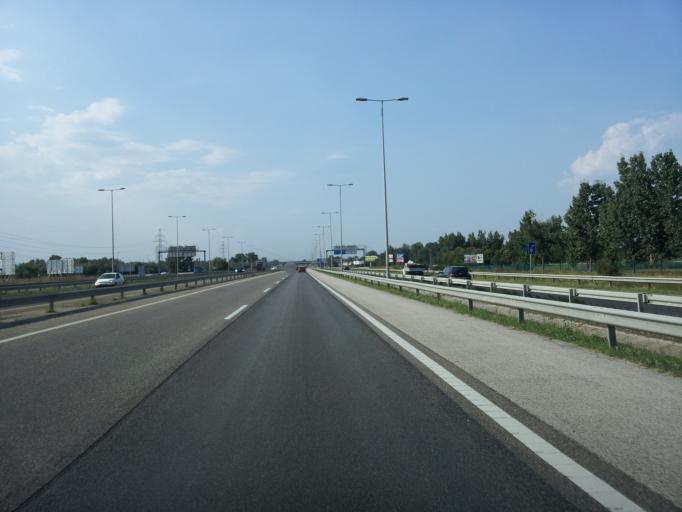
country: HU
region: Budapest
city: Budapest XVIII. keruelet
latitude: 47.4190
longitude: 19.1539
